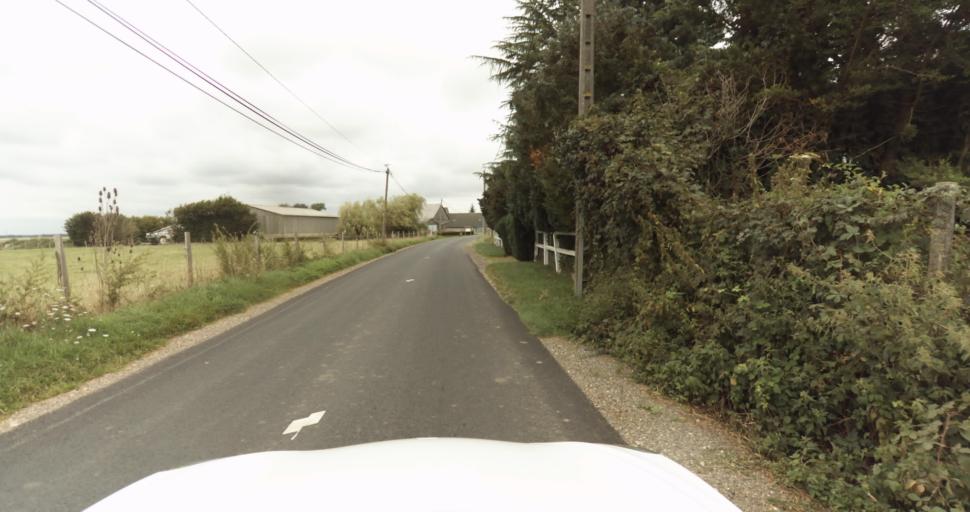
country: FR
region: Haute-Normandie
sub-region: Departement de l'Eure
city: Damville
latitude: 48.9290
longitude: 1.0830
